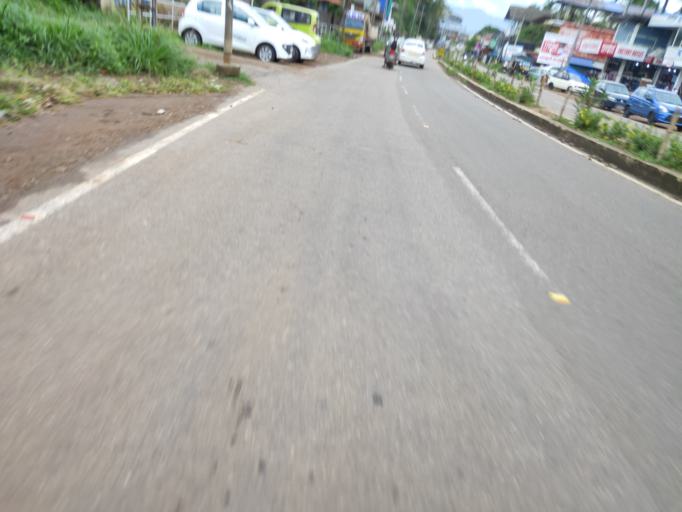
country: IN
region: Kerala
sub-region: Malappuram
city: Manjeri
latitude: 11.1976
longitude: 76.2307
